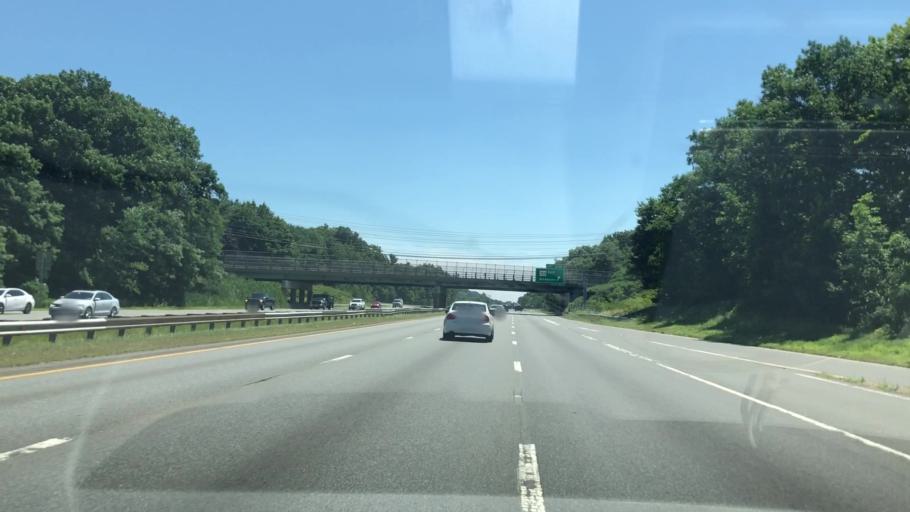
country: US
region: Massachusetts
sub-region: Essex County
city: Andover
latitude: 42.6474
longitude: -71.1869
